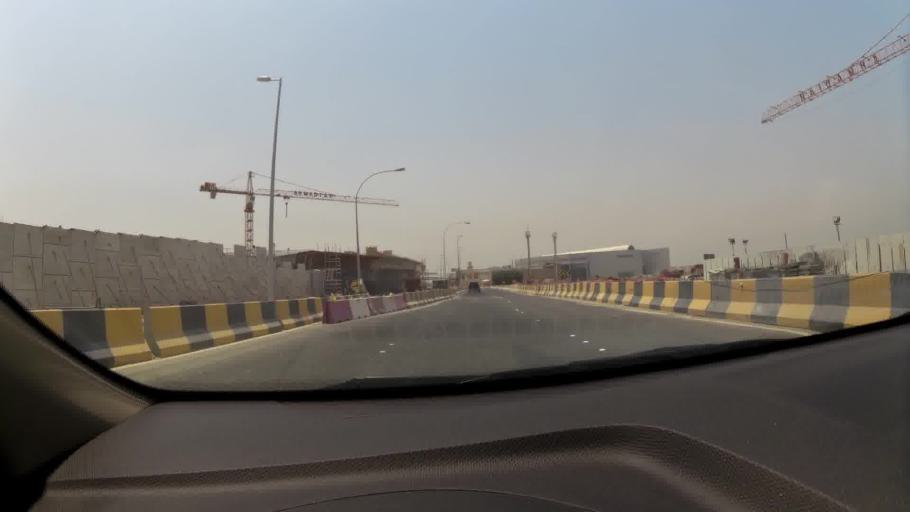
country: KW
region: Al Asimah
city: Ar Rabiyah
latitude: 29.3203
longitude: 47.8315
